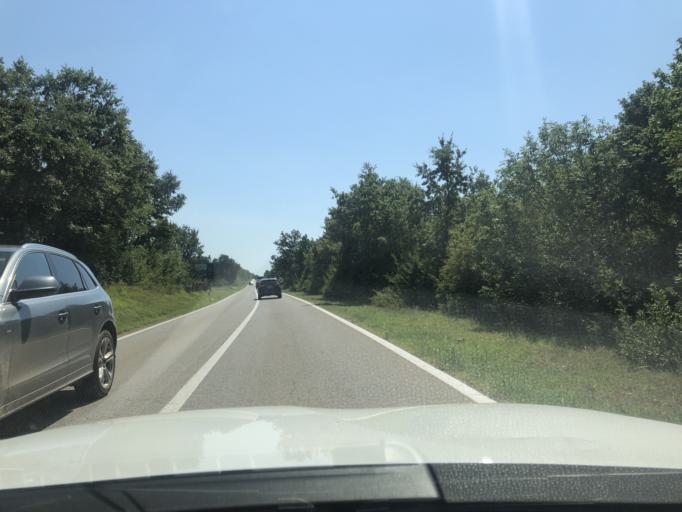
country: HR
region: Istarska
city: Vodnjan
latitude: 45.0176
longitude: 13.8044
